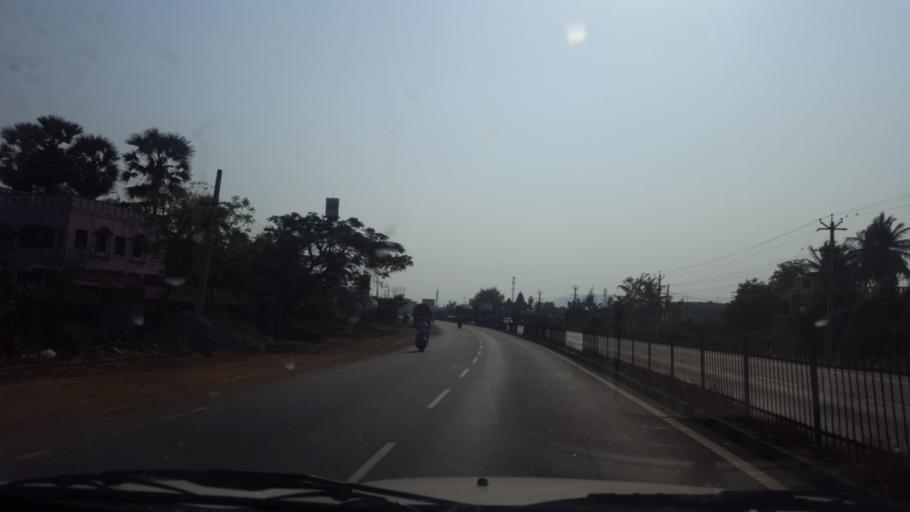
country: IN
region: Andhra Pradesh
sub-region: Vishakhapatnam
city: Anakapalle
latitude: 17.6737
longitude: 82.9710
